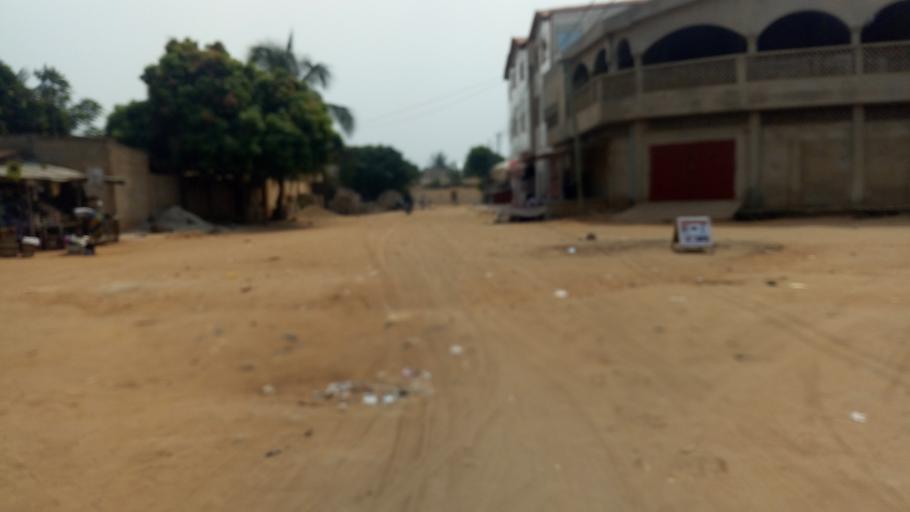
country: TG
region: Maritime
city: Lome
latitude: 6.1748
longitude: 1.1745
